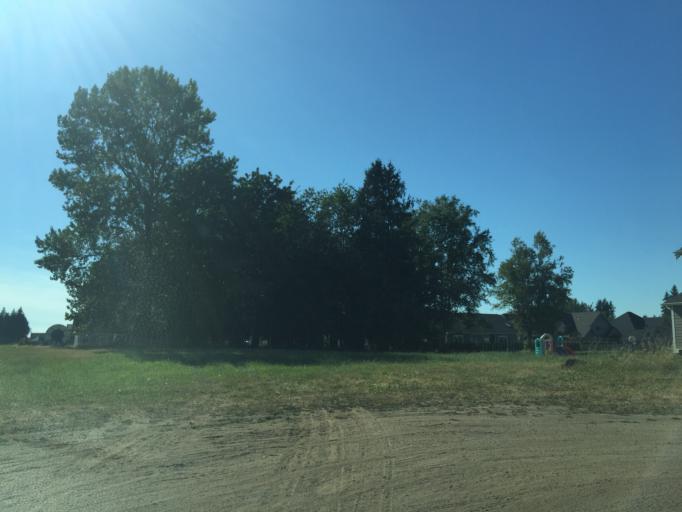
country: US
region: Washington
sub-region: Whatcom County
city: Lynden
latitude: 48.9603
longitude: -122.4124
